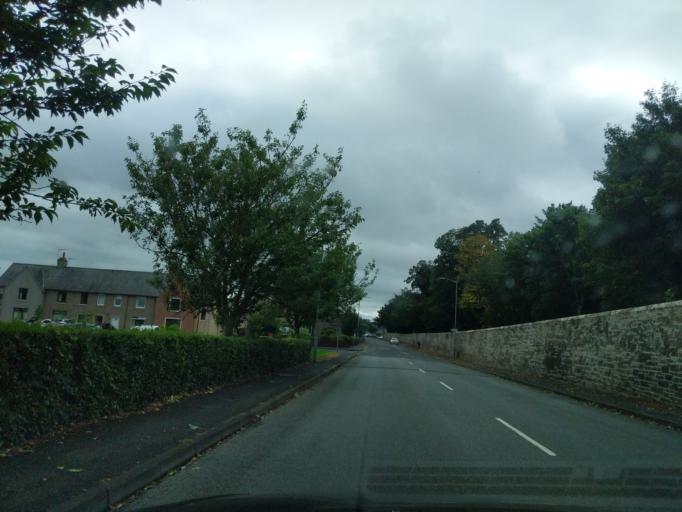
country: GB
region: Scotland
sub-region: The Scottish Borders
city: Kelso
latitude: 55.6048
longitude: -2.4440
